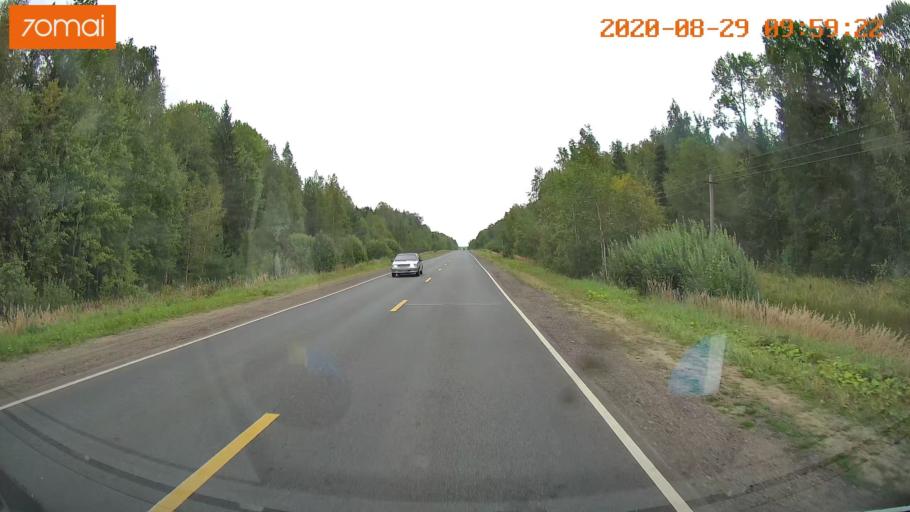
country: RU
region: Ivanovo
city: Zarechnyy
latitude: 57.4112
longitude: 42.3645
